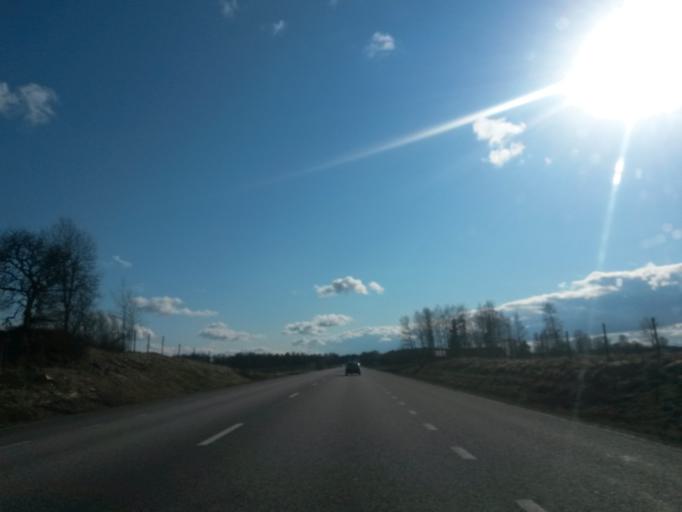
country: SE
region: Vaestra Goetaland
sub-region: Vara Kommun
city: Vara
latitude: 58.1604
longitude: 12.8795
